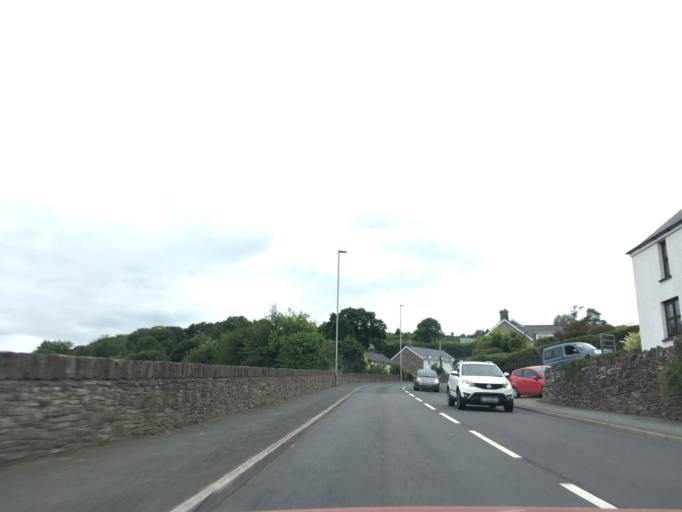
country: GB
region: Wales
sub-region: Blaenau Gwent
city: Brynmawr
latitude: 51.8903
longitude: -3.2358
